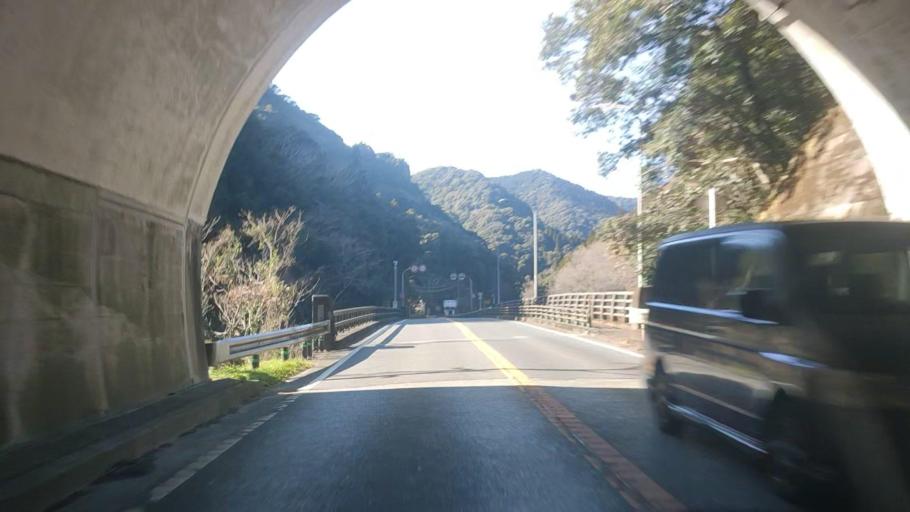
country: JP
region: Oita
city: Tsukumiura
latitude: 33.0030
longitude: 131.8015
